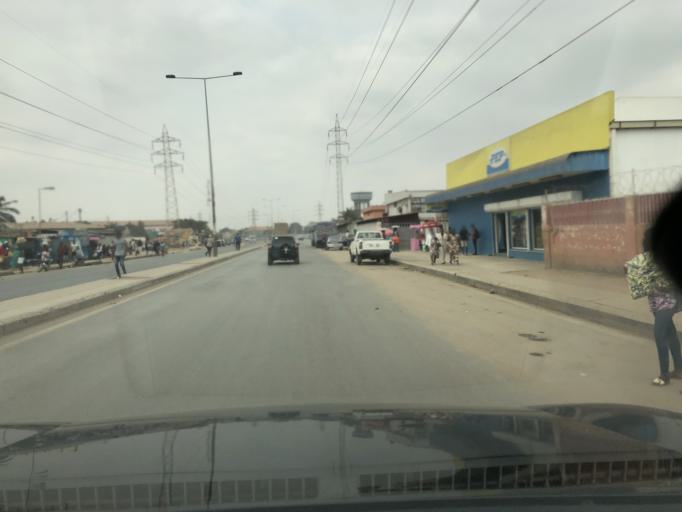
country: AO
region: Luanda
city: Luanda
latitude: -8.8182
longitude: 13.2796
